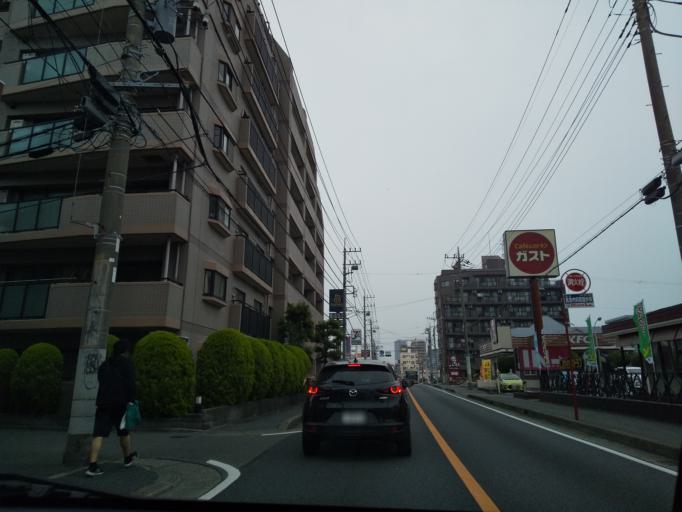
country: JP
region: Kanagawa
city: Zama
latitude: 35.5042
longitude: 139.4108
